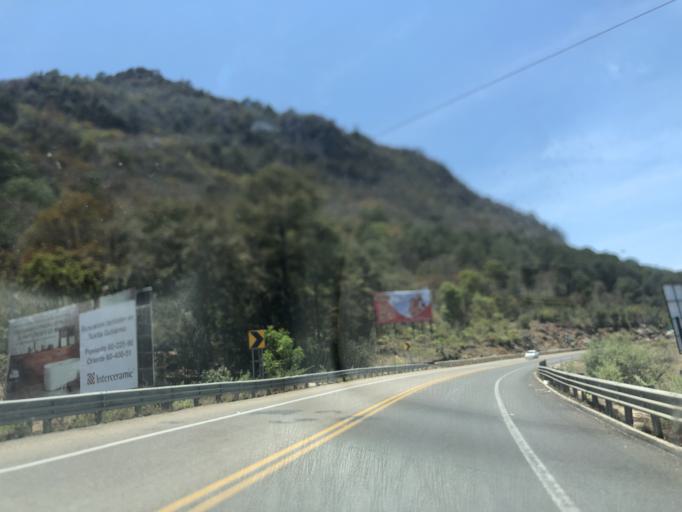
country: MX
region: Chiapas
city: San Cristobal de las Casas
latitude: 16.7170
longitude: -92.6580
